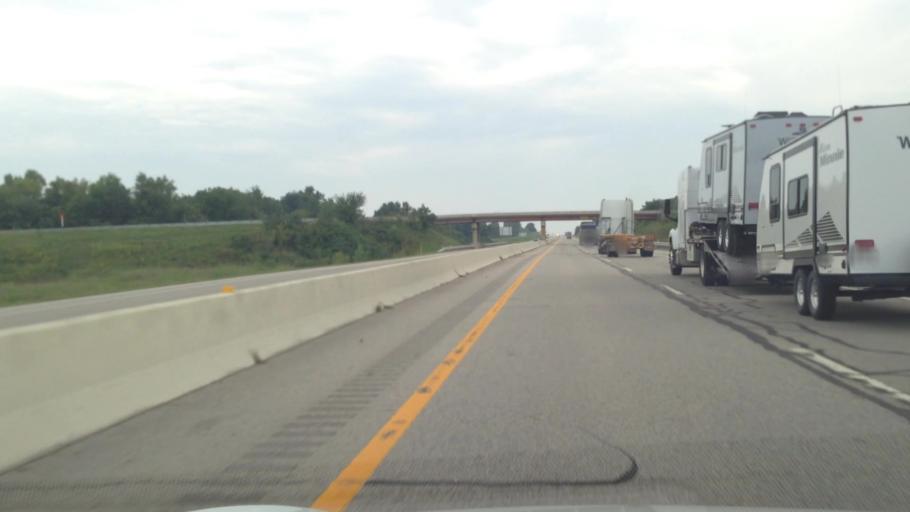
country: US
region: Oklahoma
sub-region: Ottawa County
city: Miami
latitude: 36.8461
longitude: -94.8587
